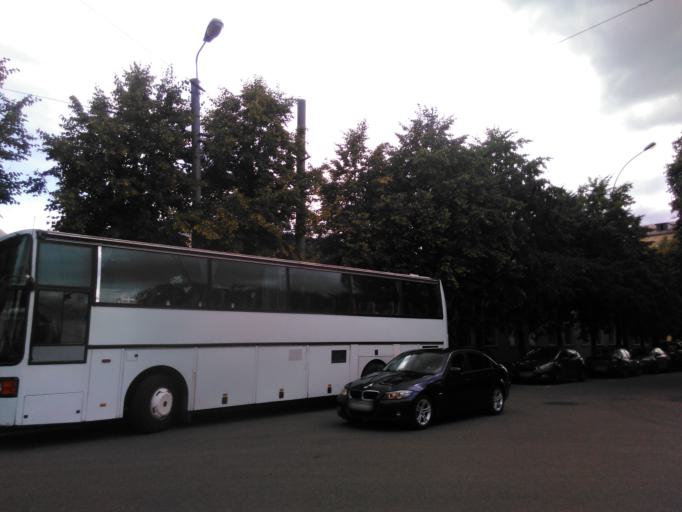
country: RU
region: Moscow
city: Zamoskvorech'ye
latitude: 55.7116
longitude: 37.6328
